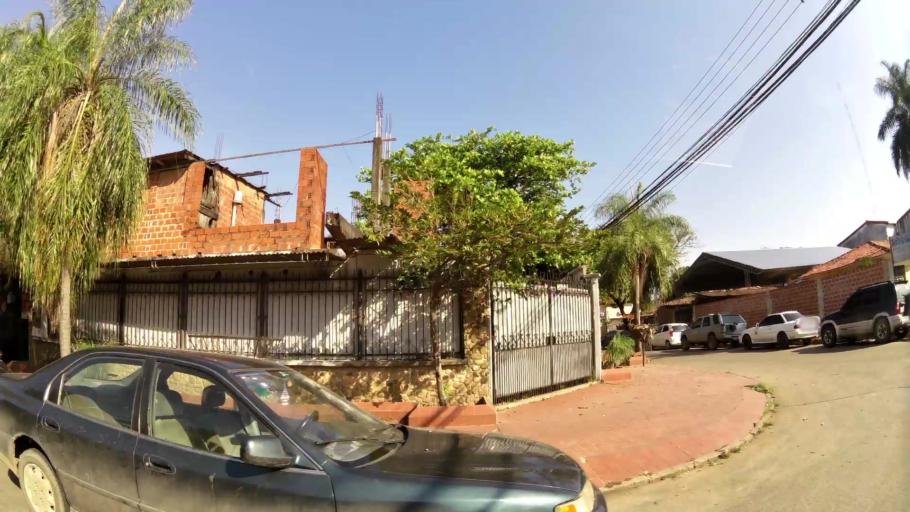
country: BO
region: Santa Cruz
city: Santa Cruz de la Sierra
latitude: -17.7831
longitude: -63.1625
